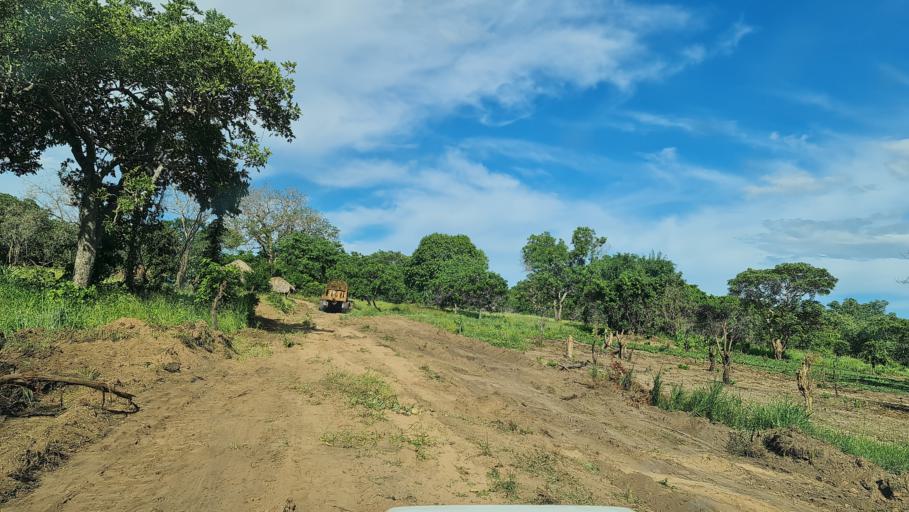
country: MZ
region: Nampula
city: Ilha de Mocambique
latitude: -15.5051
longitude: 40.1514
